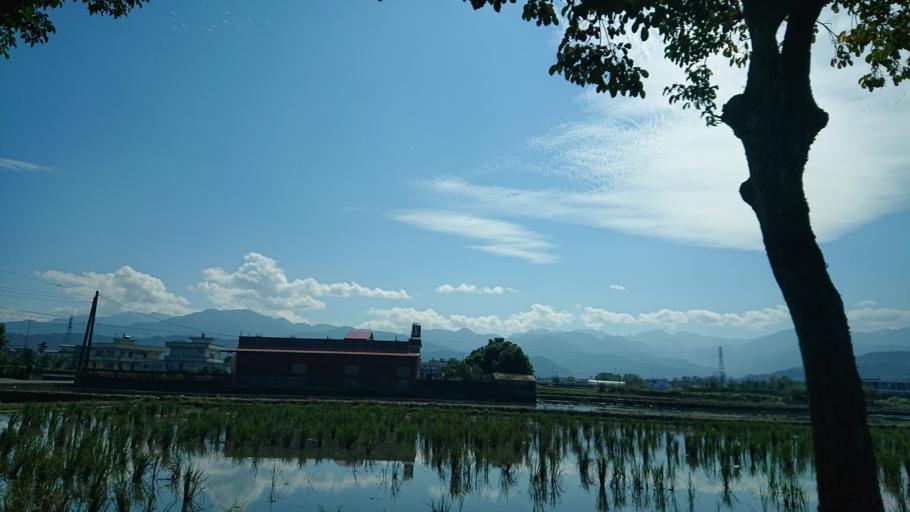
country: TW
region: Taiwan
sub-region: Yilan
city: Yilan
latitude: 24.6698
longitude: 121.7220
